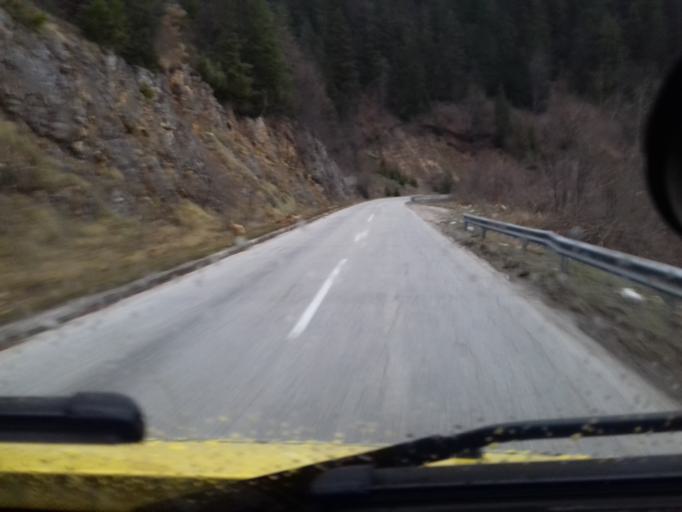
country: BA
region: Federation of Bosnia and Herzegovina
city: Turbe
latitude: 44.2851
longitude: 17.5058
